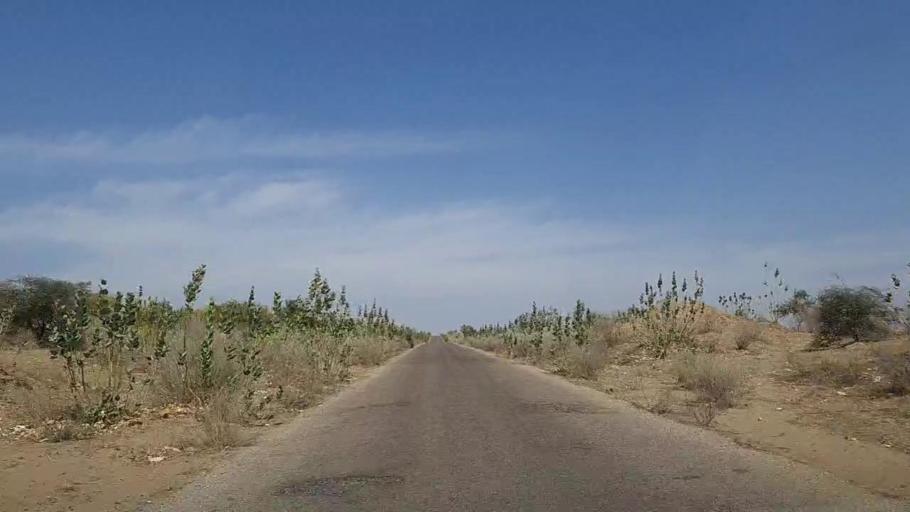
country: PK
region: Sindh
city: Umarkot
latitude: 25.1185
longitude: 69.9997
